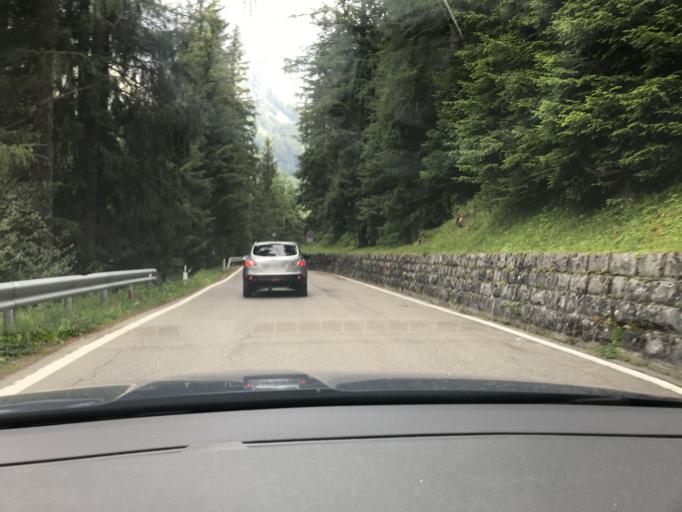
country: IT
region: Trentino-Alto Adige
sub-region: Bolzano
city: San Martino
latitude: 46.8849
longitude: 12.1701
